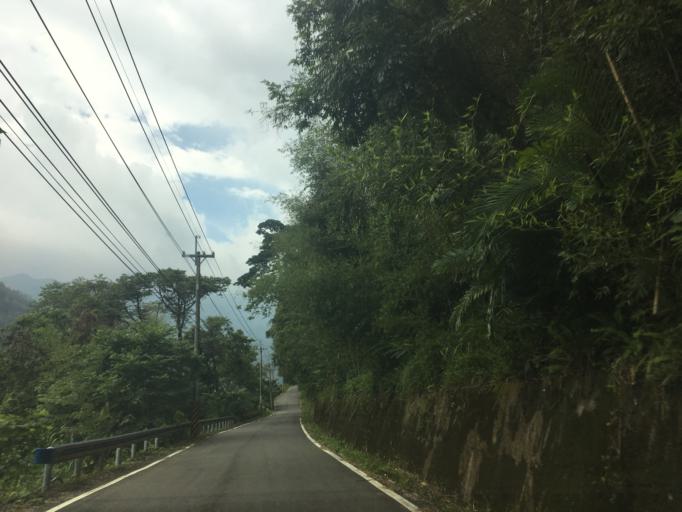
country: TW
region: Taiwan
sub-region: Miaoli
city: Miaoli
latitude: 24.3633
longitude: 120.9602
